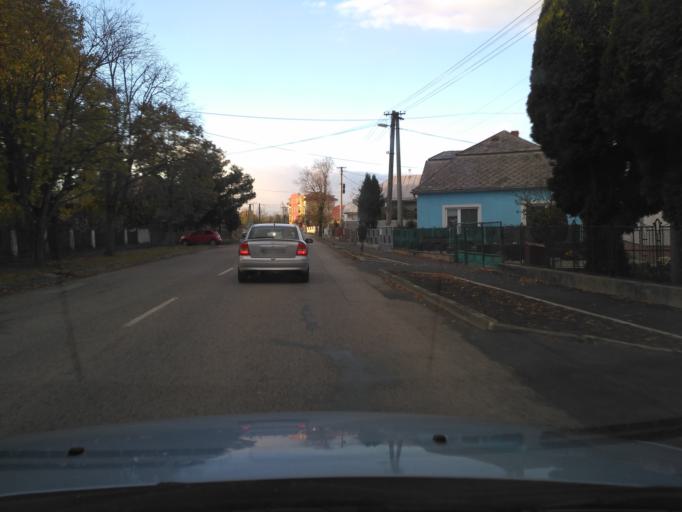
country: SK
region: Kosicky
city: Trebisov
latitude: 48.6515
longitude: 21.6774
